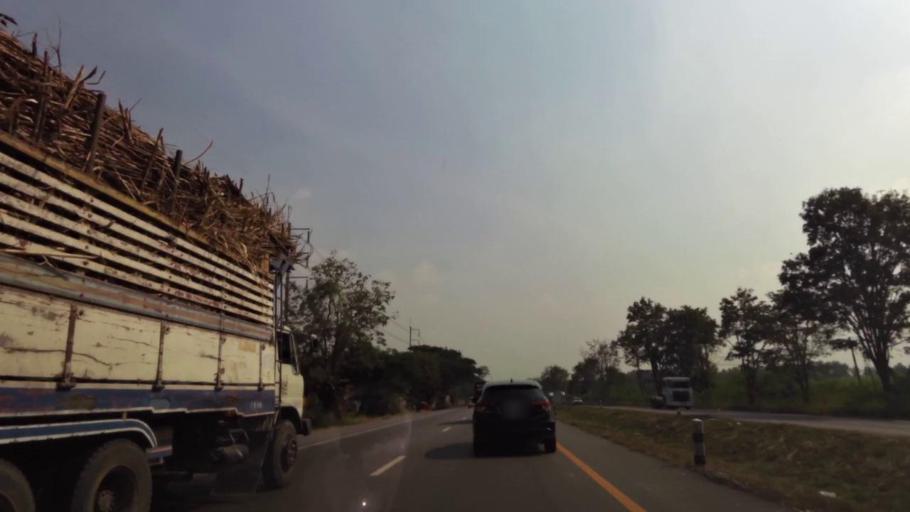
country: TH
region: Chon Buri
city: Ban Bueng
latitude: 13.2698
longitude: 101.1916
